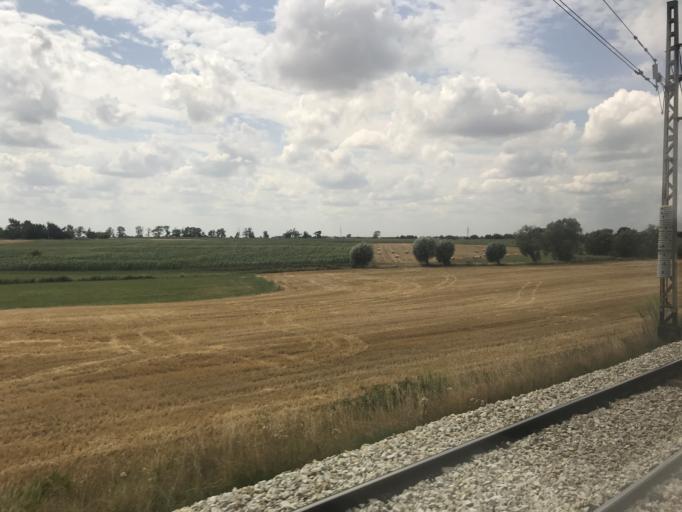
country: PL
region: Greater Poland Voivodeship
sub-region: Powiat poznanski
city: Buk
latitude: 52.3470
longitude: 16.5542
